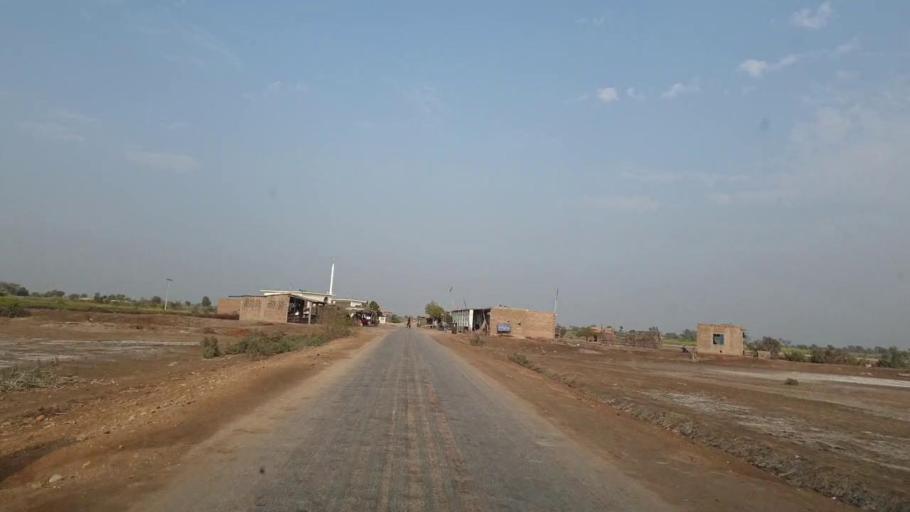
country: PK
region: Sindh
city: Pithoro
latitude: 25.5600
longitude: 69.2260
